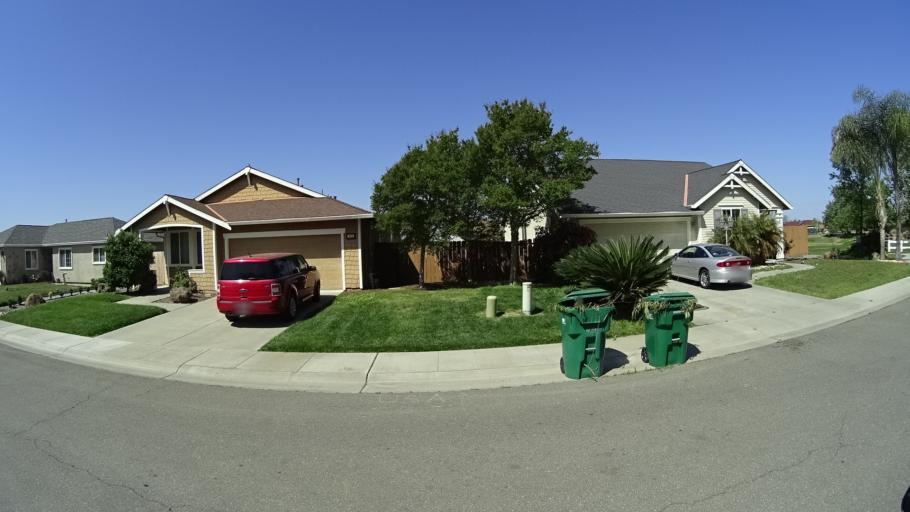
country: US
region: California
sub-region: Glenn County
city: Orland
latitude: 39.7605
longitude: -122.1976
